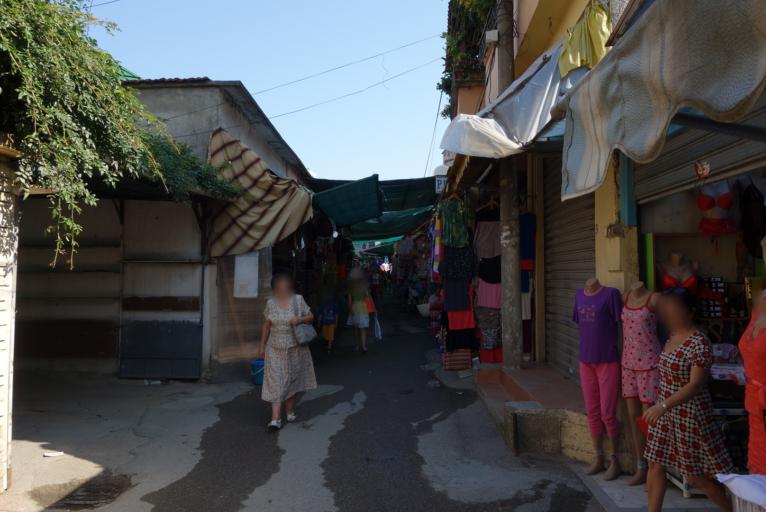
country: AL
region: Tirane
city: Tirana
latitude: 41.3260
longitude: 19.8139
